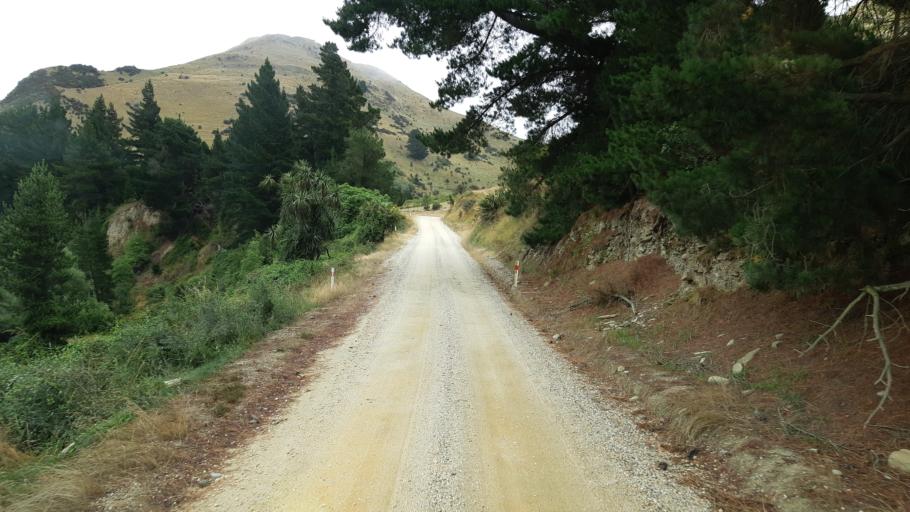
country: NZ
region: Otago
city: Oamaru
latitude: -44.9531
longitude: 170.4708
